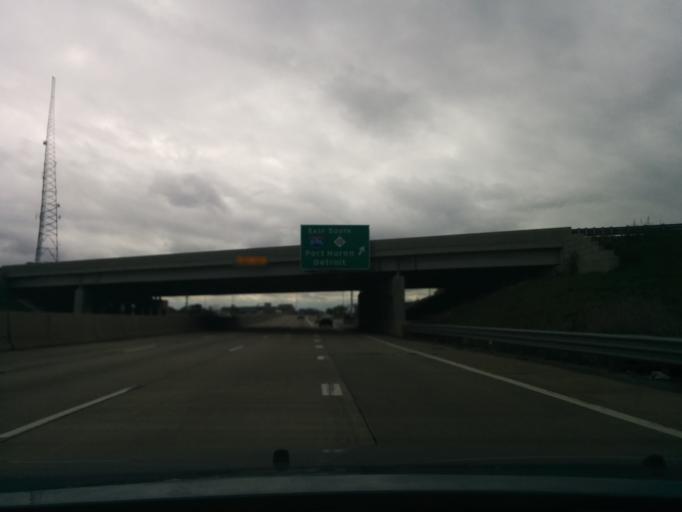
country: US
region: Michigan
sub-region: Oakland County
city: Bingham Farms
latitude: 42.4922
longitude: -83.2850
